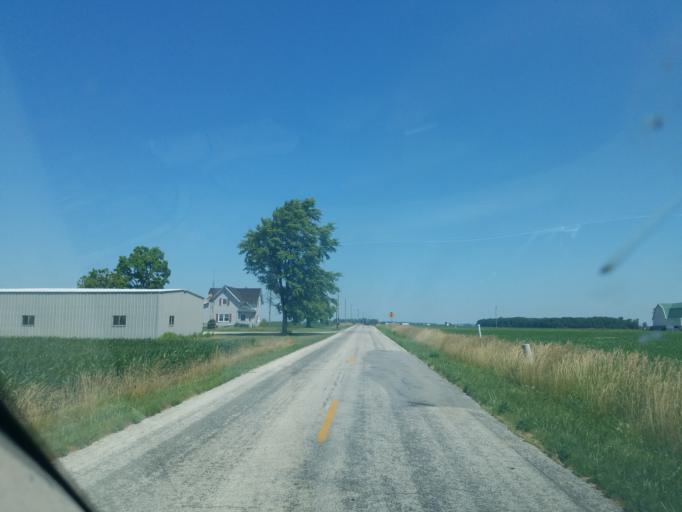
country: US
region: Ohio
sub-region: Mercer County
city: Rockford
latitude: 40.6310
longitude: -84.7087
